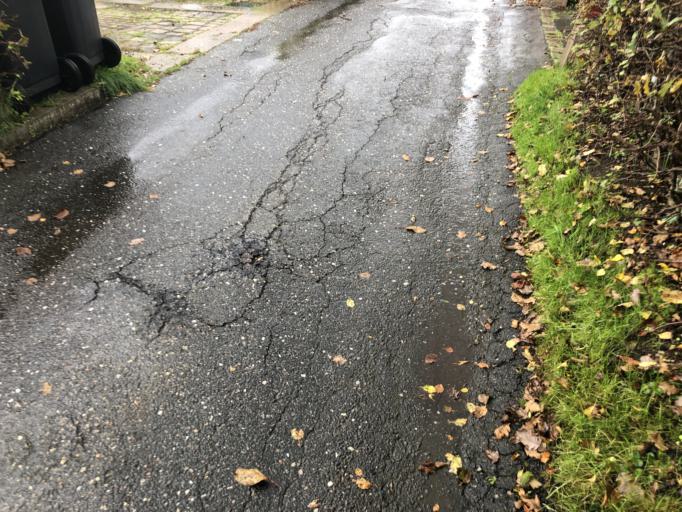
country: SE
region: Vaestra Goetaland
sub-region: Molndal
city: Moelndal
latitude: 57.6512
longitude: 12.0352
